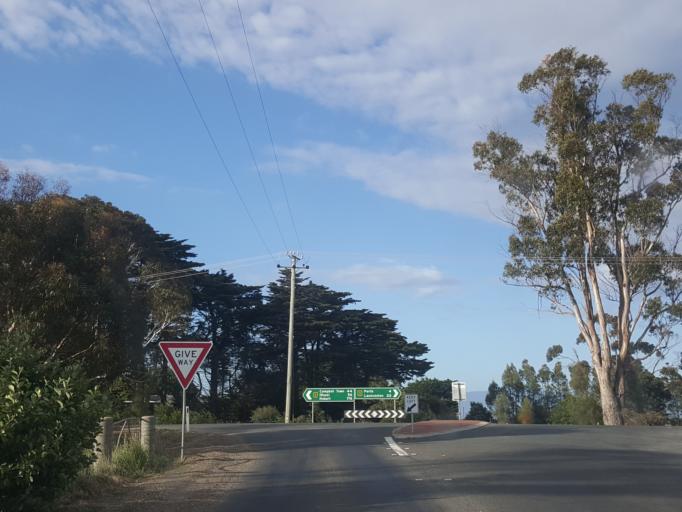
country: AU
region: Tasmania
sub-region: Northern Midlands
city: Evandale
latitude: -41.5974
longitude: 147.2136
